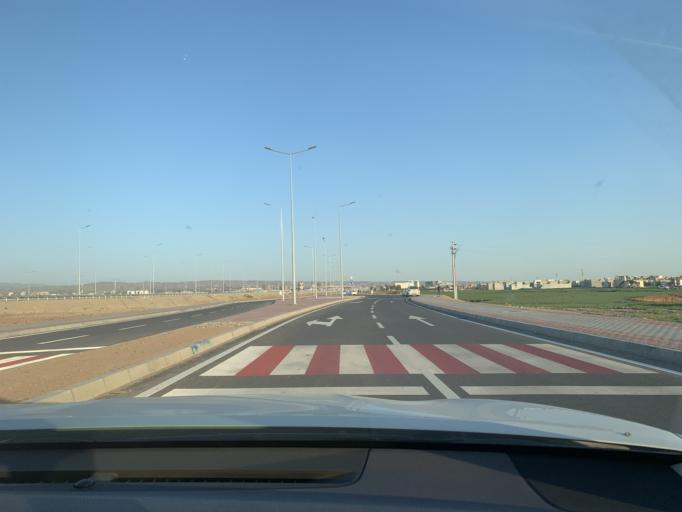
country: IQ
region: Arbil
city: Erbil
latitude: 36.2829
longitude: 44.0562
